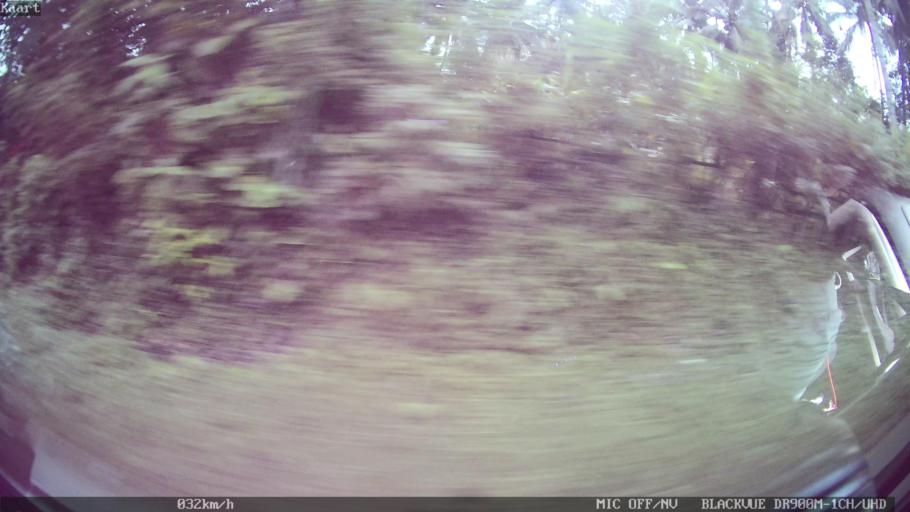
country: ID
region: Bali
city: Pegongan
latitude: -8.4761
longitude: 115.2313
